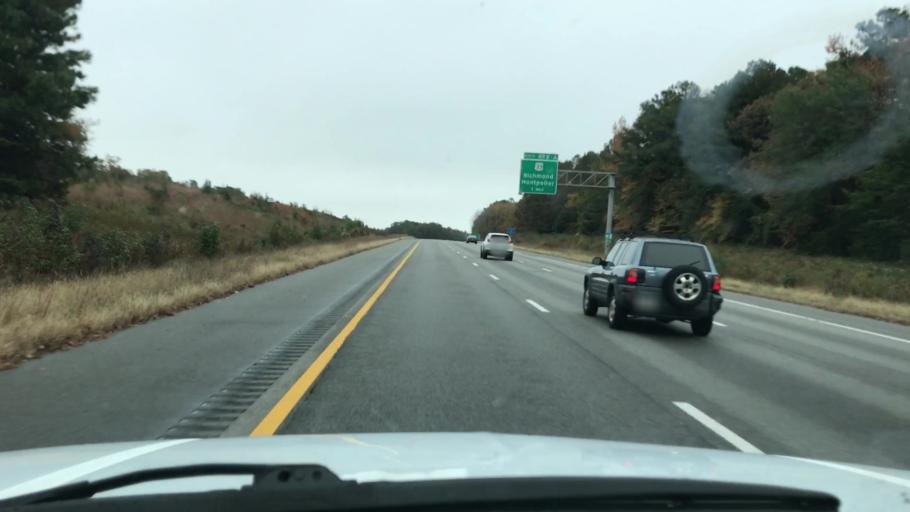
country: US
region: Virginia
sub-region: Henrico County
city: Wyndham
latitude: 37.6755
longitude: -77.5648
